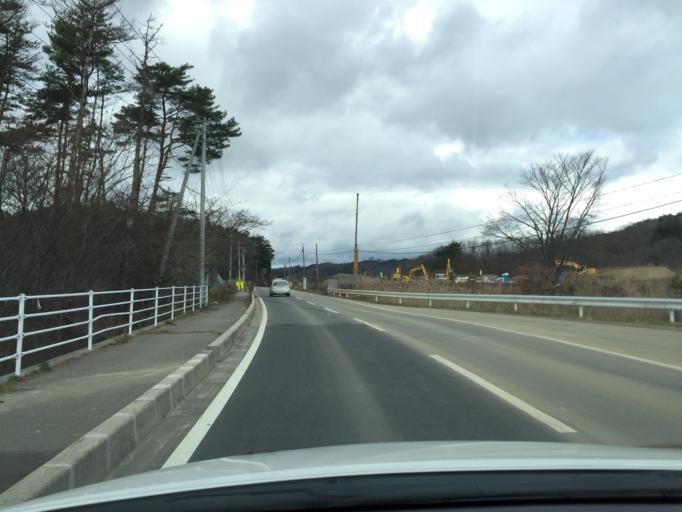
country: JP
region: Fukushima
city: Yanagawamachi-saiwaicho
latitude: 37.7083
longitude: 140.6954
